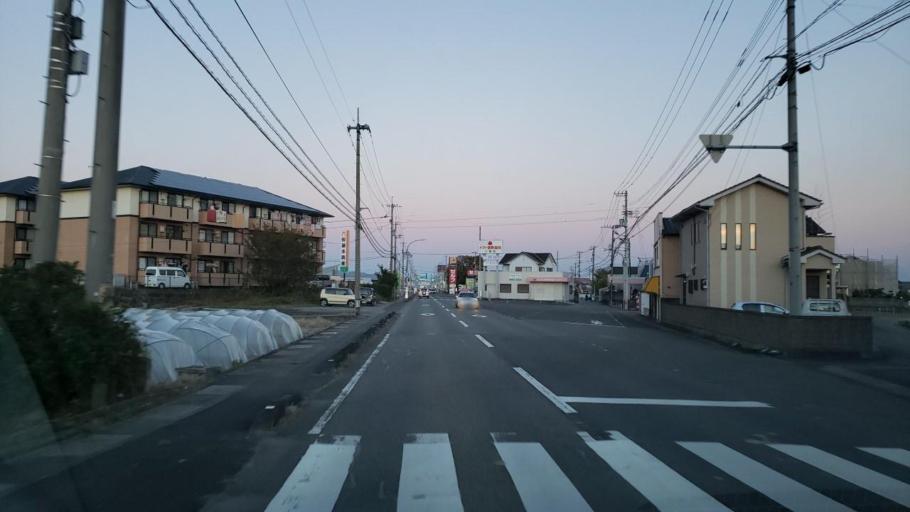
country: JP
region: Tokushima
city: Ishii
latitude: 34.1153
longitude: 134.4218
